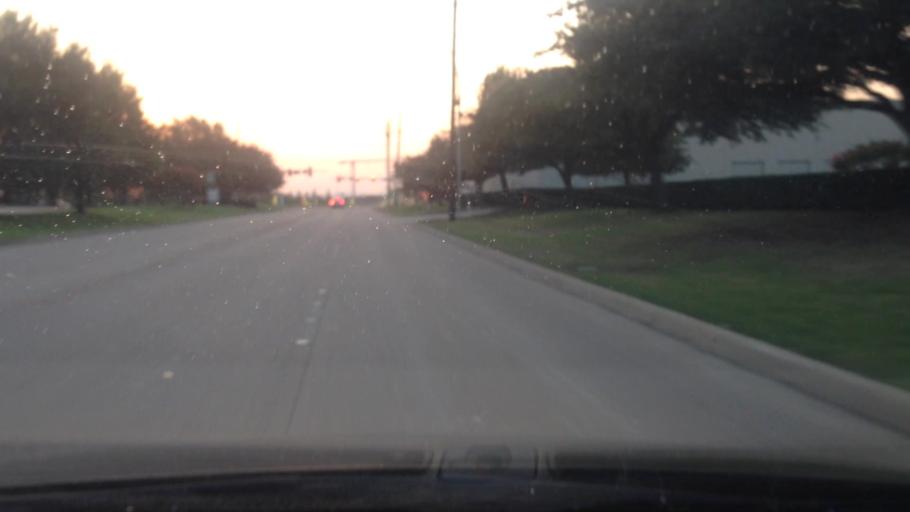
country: US
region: Texas
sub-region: Dallas County
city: Coppell
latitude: 32.9399
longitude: -96.9956
